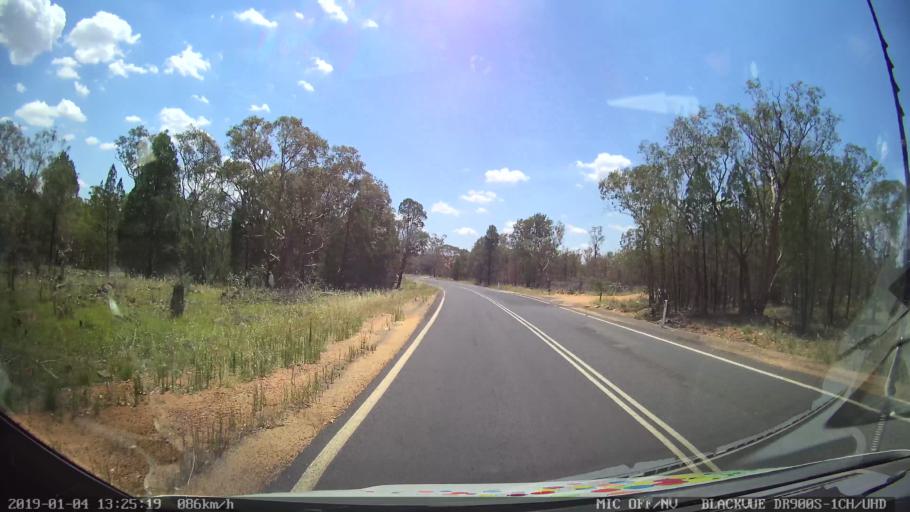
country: AU
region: New South Wales
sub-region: Parkes
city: Peak Hill
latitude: -32.6946
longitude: 148.5556
